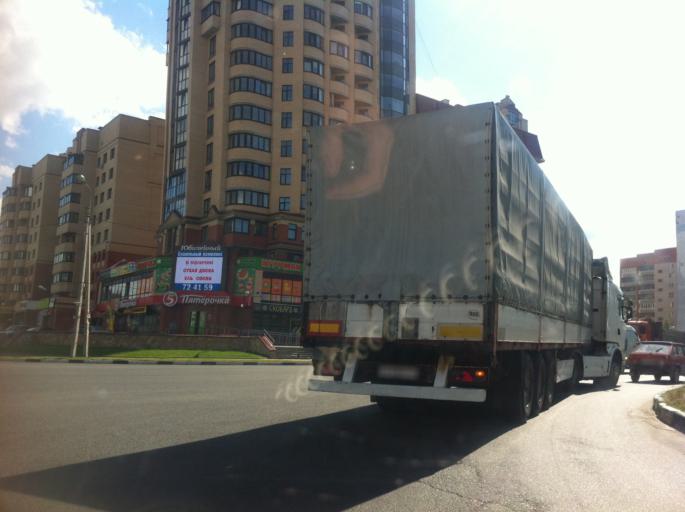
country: RU
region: Pskov
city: Pskov
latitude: 57.8142
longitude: 28.2933
